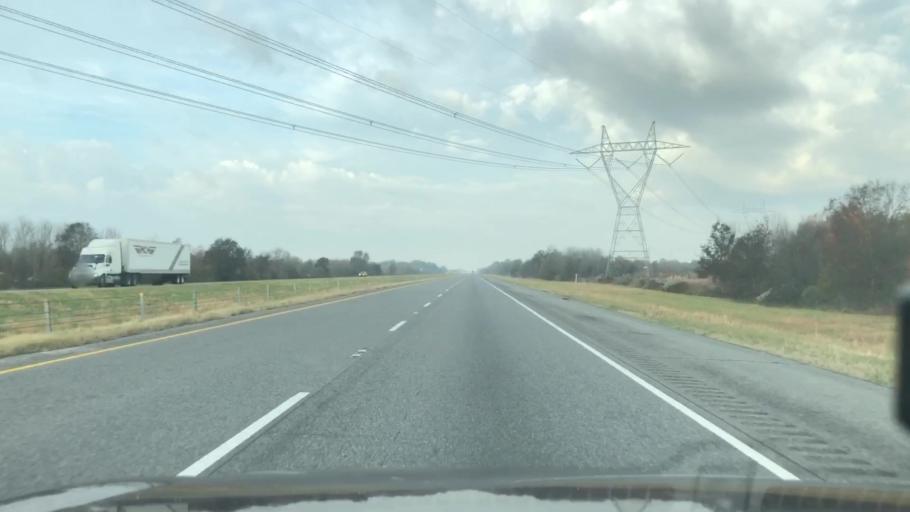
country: US
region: Louisiana
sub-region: Madison Parish
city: Tallulah
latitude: 32.4198
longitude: -91.3054
